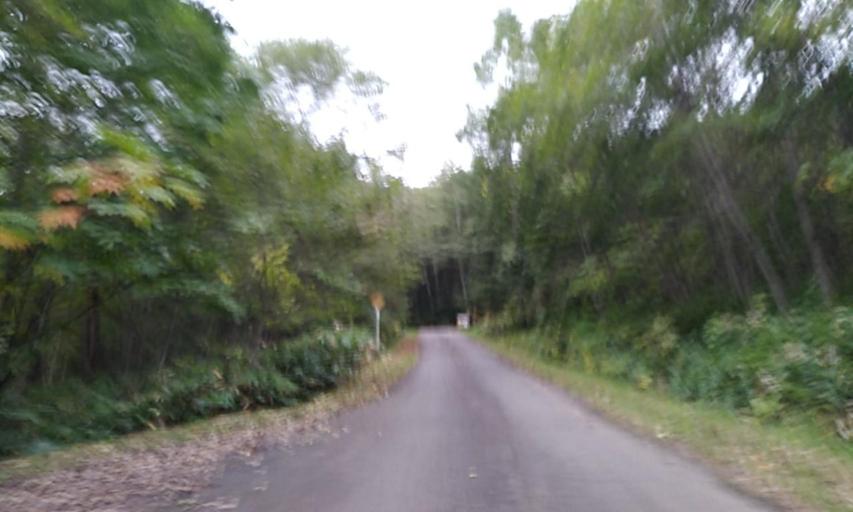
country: JP
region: Hokkaido
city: Obihiro
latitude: 42.8261
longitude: 142.9866
